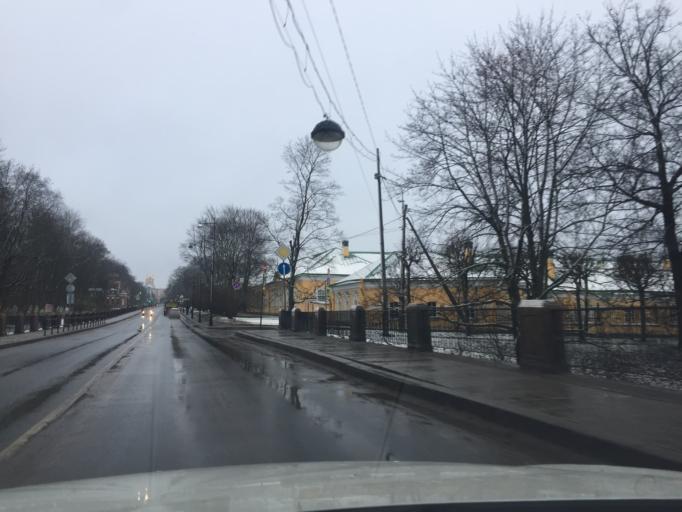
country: RU
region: St.-Petersburg
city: Pushkin
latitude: 59.7134
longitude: 30.4092
